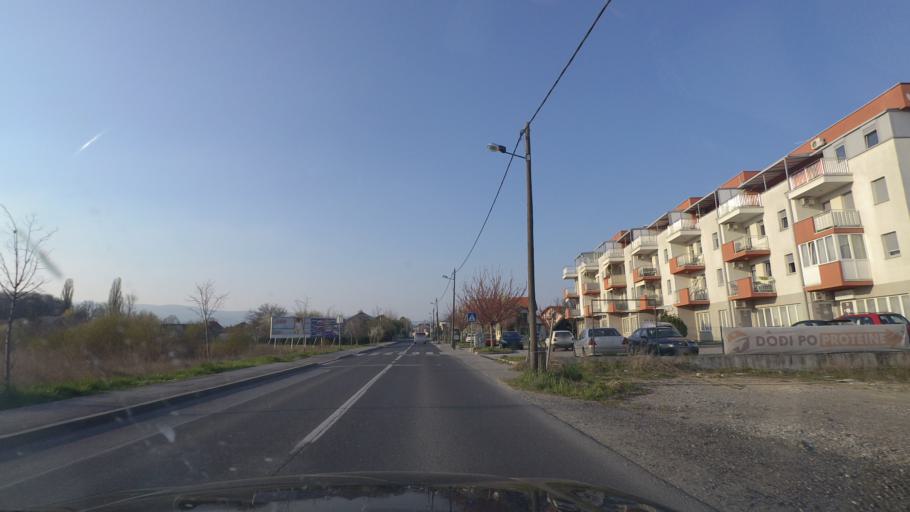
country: HR
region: Grad Zagreb
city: Dubrava
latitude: 45.8146
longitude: 16.0661
